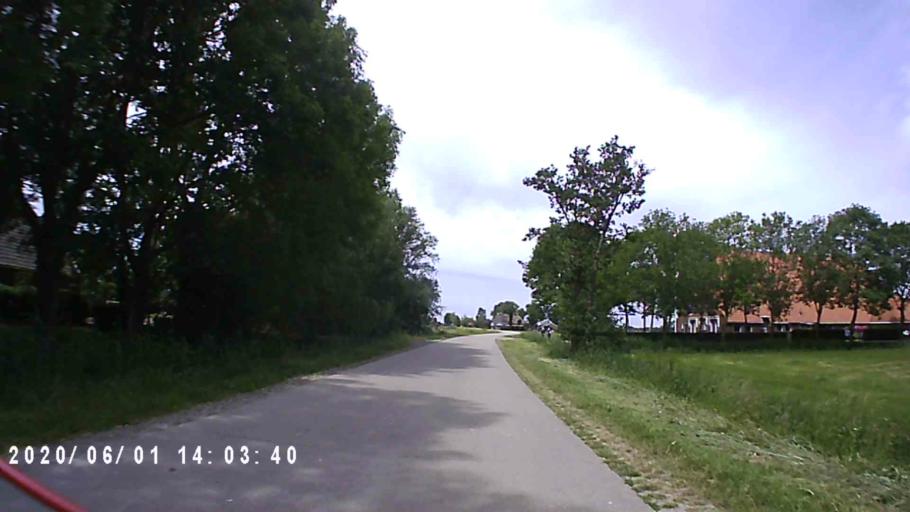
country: NL
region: Friesland
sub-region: Gemeente Littenseradiel
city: Winsum
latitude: 53.1124
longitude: 5.6350
